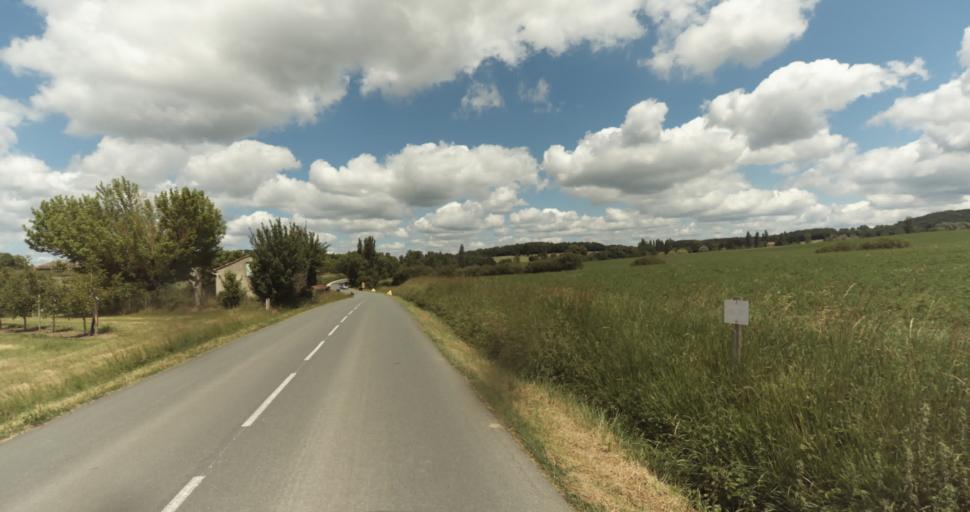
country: FR
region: Aquitaine
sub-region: Departement du Lot-et-Garonne
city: Villereal
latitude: 44.6995
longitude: 0.7499
